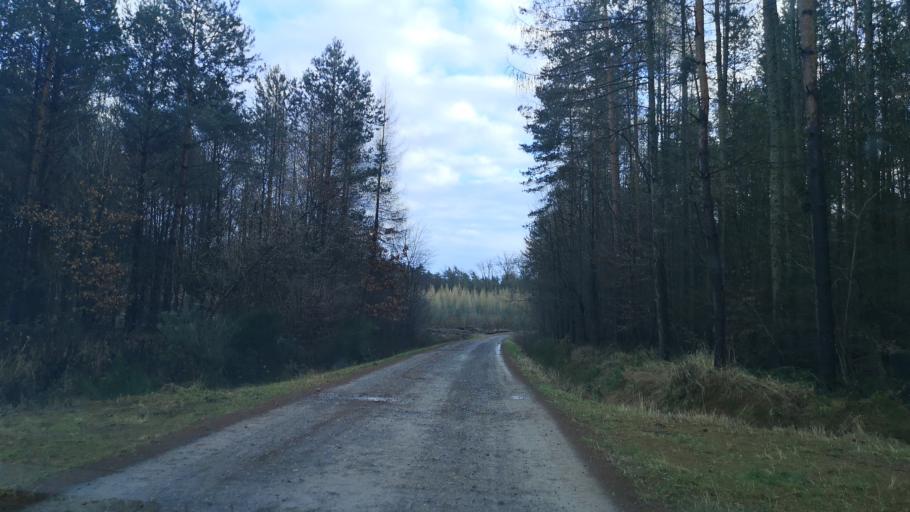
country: PL
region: Subcarpathian Voivodeship
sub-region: Powiat lezajski
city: Piskorowice
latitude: 50.2521
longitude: 22.5678
